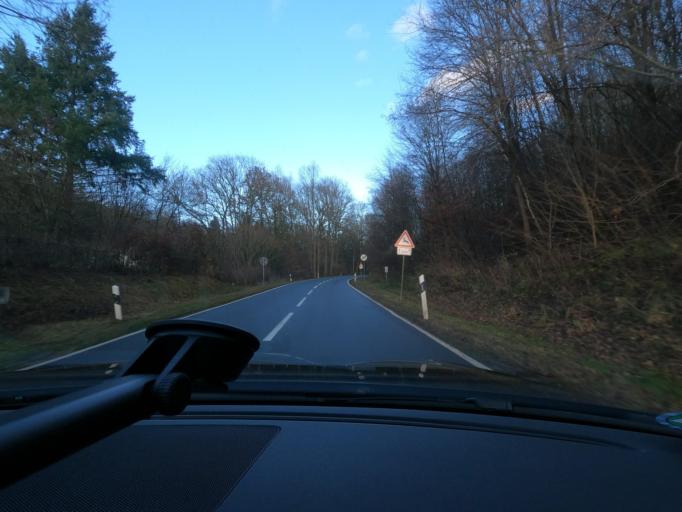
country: DE
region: Lower Saxony
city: Rhumspringe
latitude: 51.5917
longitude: 10.3104
